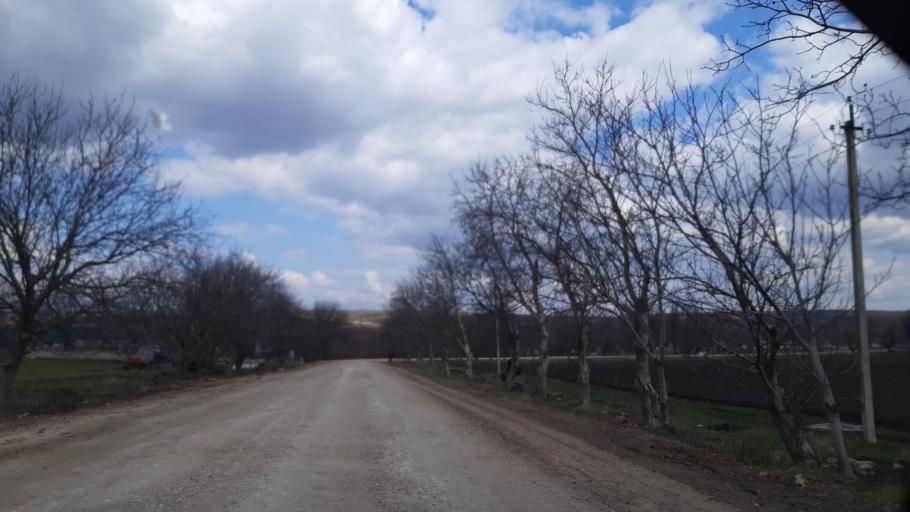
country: MD
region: Laloveni
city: Ialoveni
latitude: 46.8912
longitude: 28.7247
